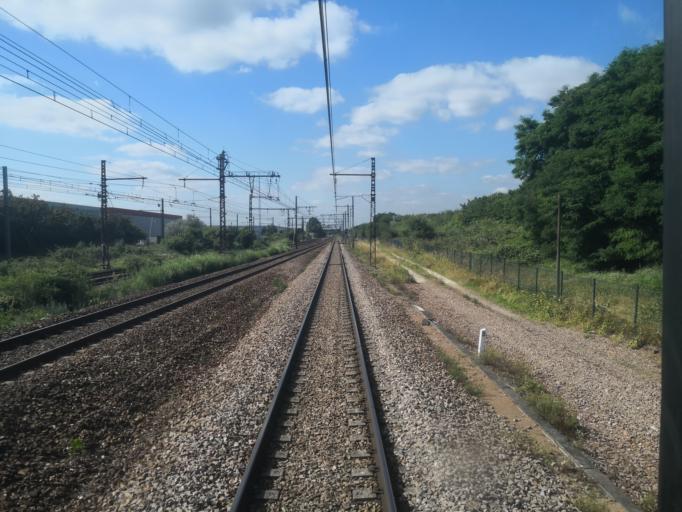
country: FR
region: Ile-de-France
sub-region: Departement de Seine-et-Marne
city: Lieusaint
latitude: 48.6471
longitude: 2.5611
